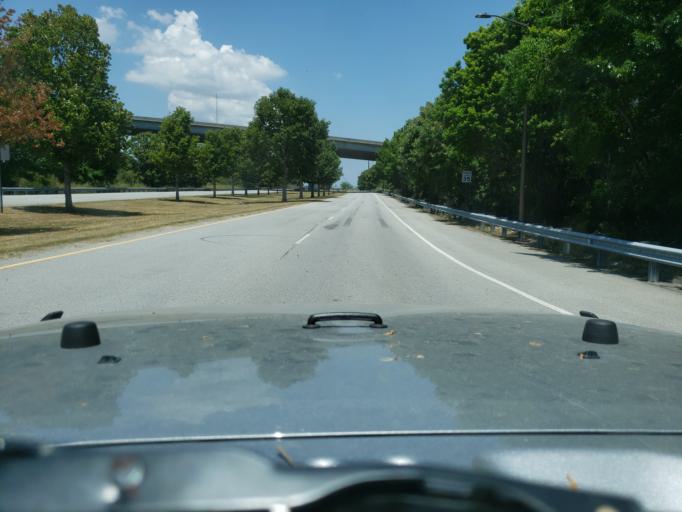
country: US
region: Georgia
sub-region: Chatham County
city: Savannah
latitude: 32.0945
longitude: -81.0920
